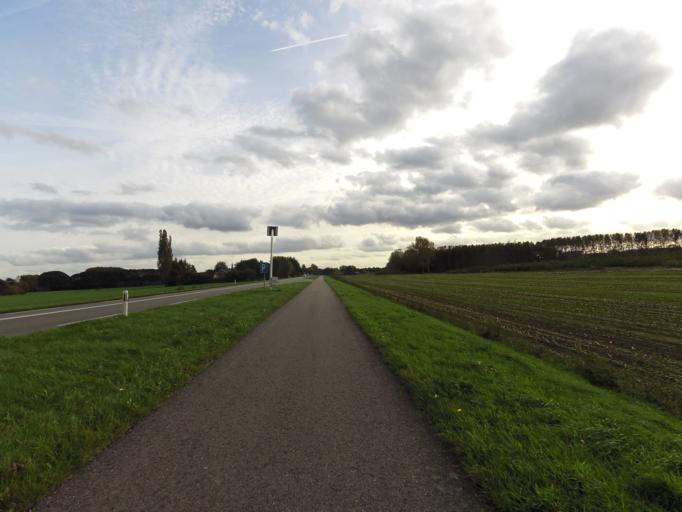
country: NL
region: Gelderland
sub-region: Gemeente Bronckhorst
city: Baak
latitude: 52.0866
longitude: 6.2224
